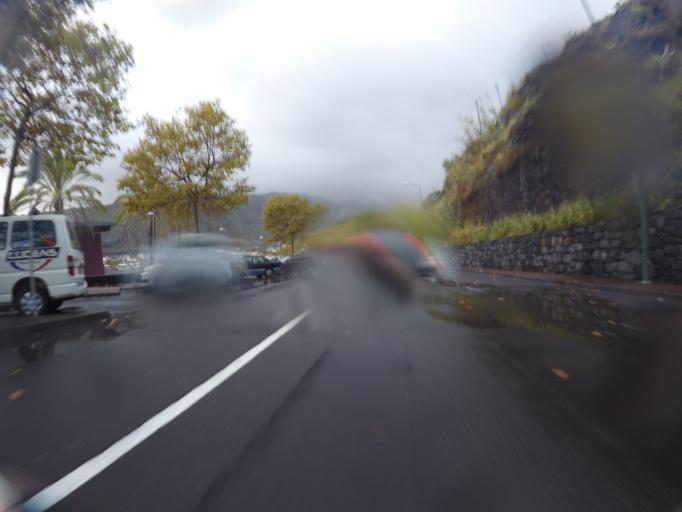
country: PT
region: Madeira
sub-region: Machico
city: Machico
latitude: 32.7188
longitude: -16.7600
